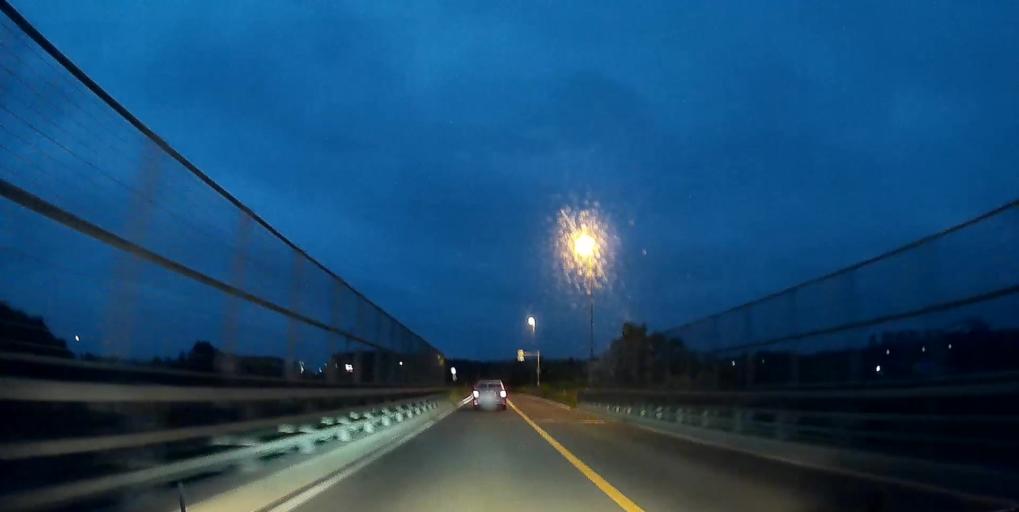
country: JP
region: Hokkaido
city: Nanae
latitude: 42.2100
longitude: 140.3951
